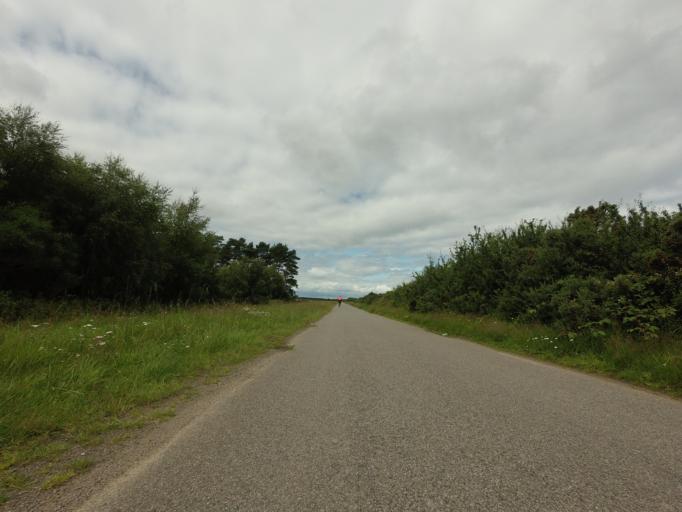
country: GB
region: Scotland
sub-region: Moray
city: Kinloss
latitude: 57.6286
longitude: -3.5939
